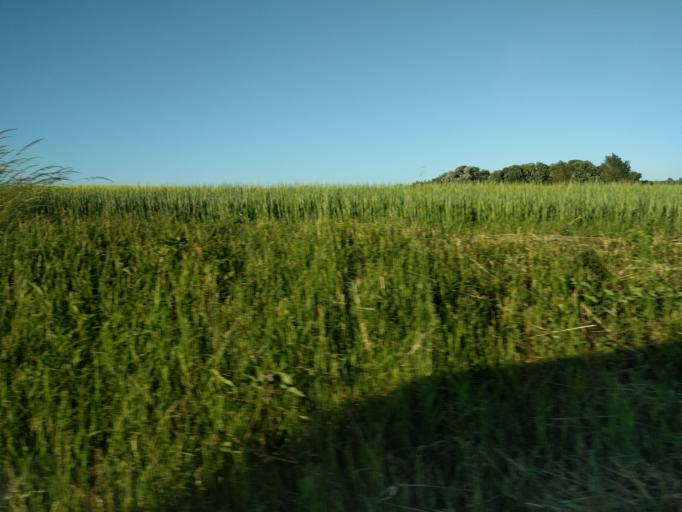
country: DK
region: South Denmark
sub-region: Kerteminde Kommune
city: Kerteminde
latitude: 55.5499
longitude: 10.6565
